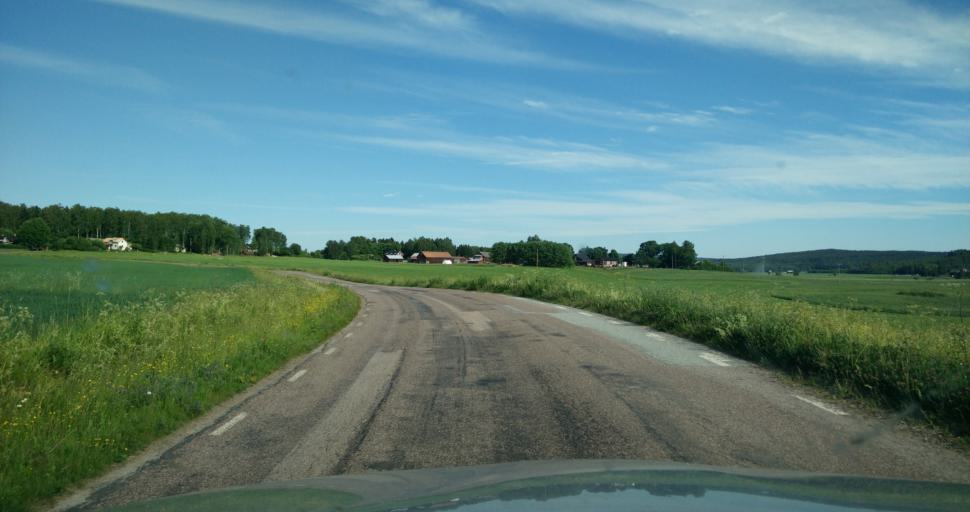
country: SE
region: Dalarna
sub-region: Hedemora Kommun
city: Langshyttan
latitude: 60.3869
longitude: 15.9761
